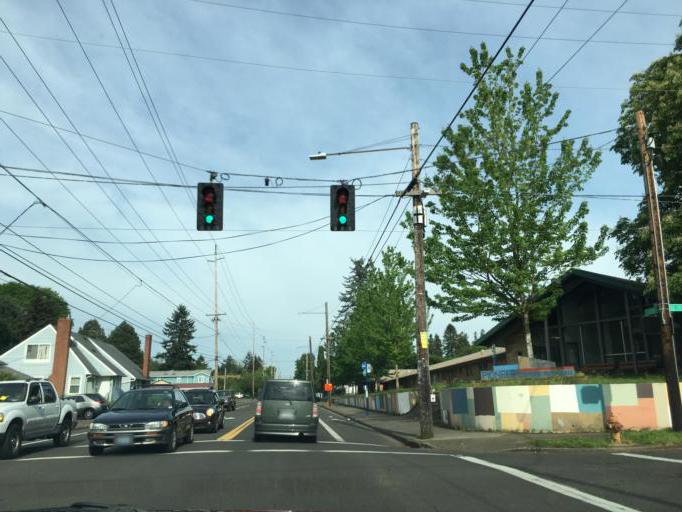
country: US
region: Oregon
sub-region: Multnomah County
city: Lents
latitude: 45.5054
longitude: -122.5899
